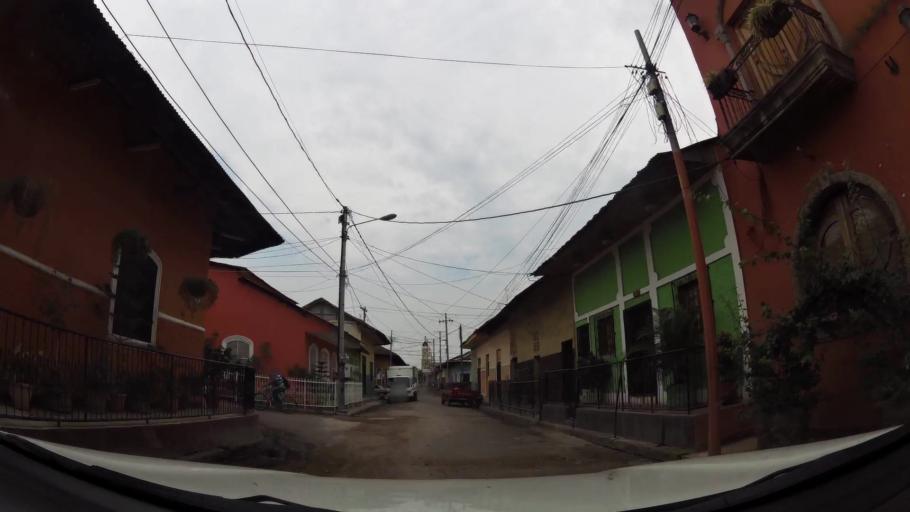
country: NI
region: Granada
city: Granada
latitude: 11.9267
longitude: -85.9534
